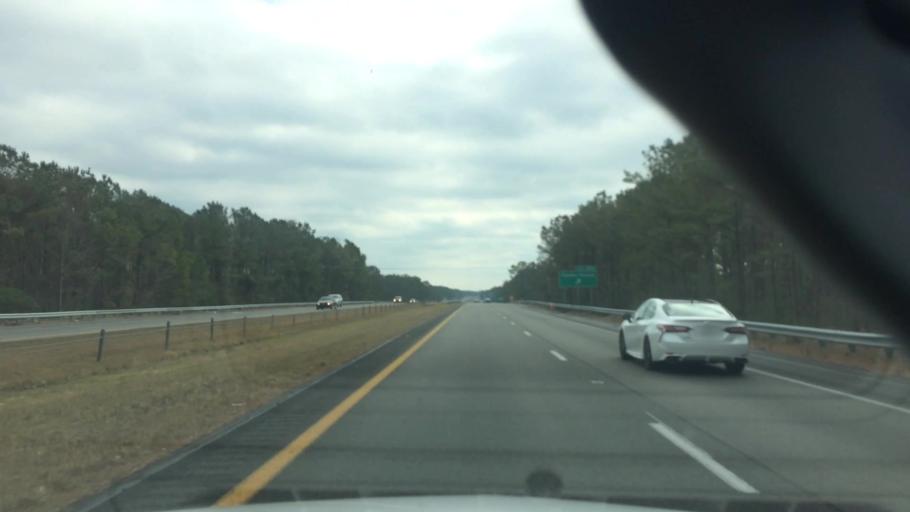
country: US
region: North Carolina
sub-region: New Hanover County
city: Castle Hayne
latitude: 34.3552
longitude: -77.8861
